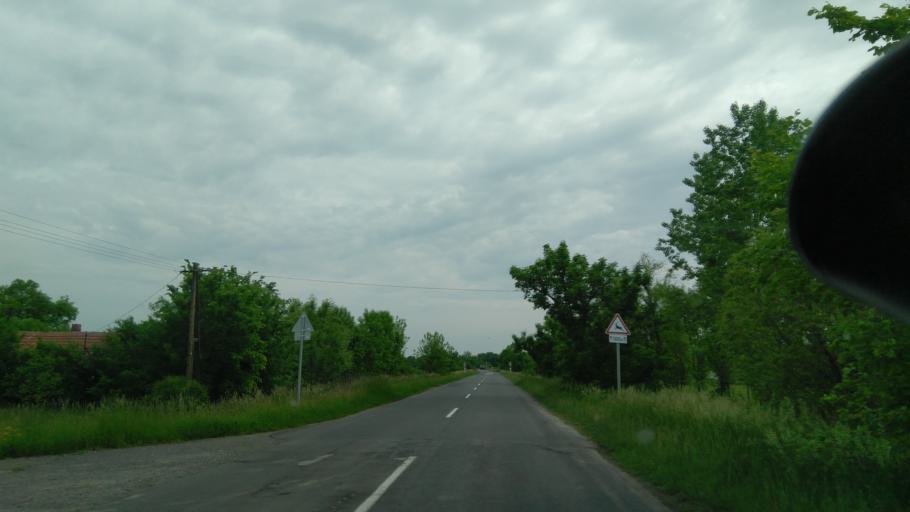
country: HU
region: Bekes
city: Szeghalom
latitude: 47.0013
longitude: 21.1751
